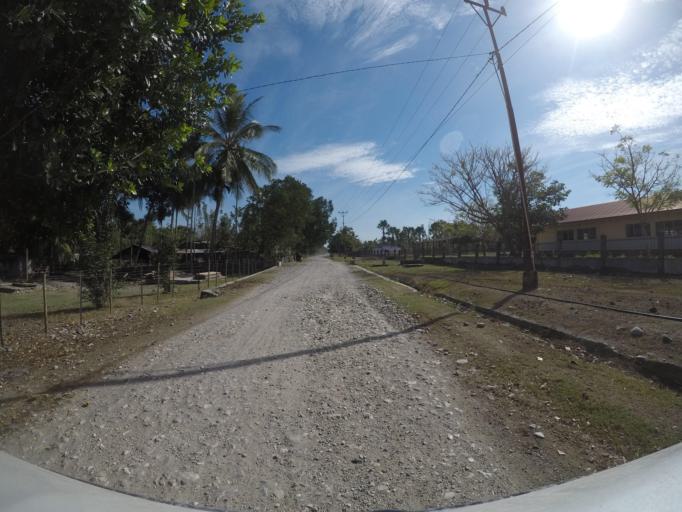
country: TL
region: Bobonaro
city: Maliana
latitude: -8.8709
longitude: 125.2128
